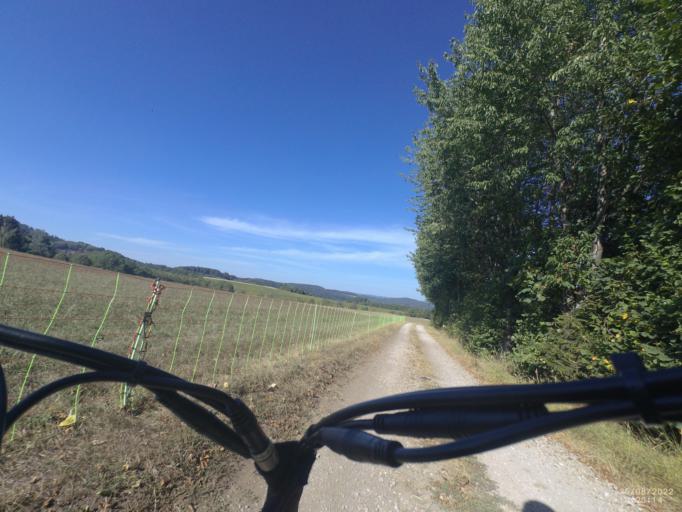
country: DE
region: Rheinland-Pfalz
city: Rockeskyll
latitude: 50.2648
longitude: 6.6929
